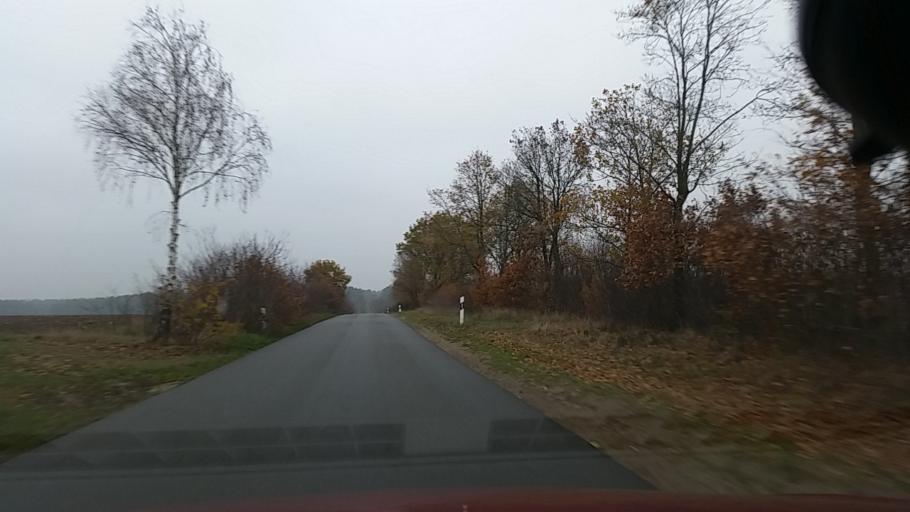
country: DE
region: Lower Saxony
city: Stadensen
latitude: 52.8134
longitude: 10.5470
